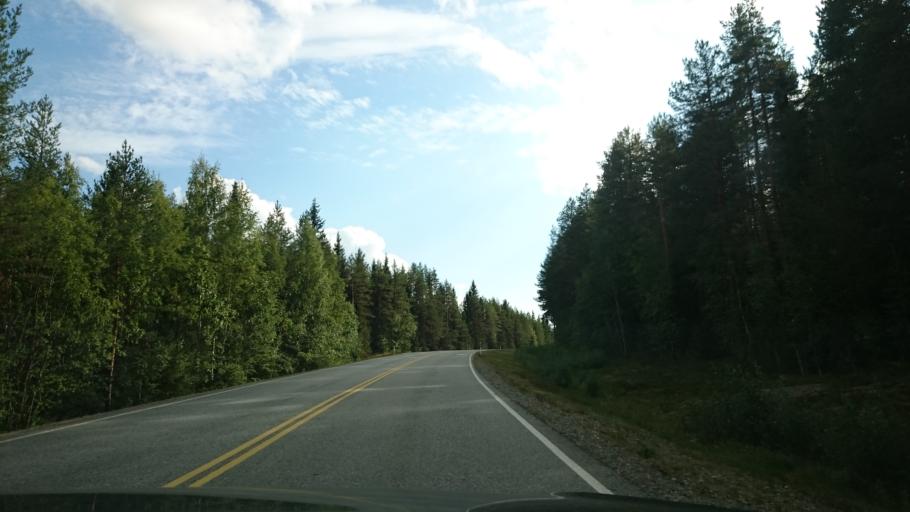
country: FI
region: Kainuu
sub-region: Kehys-Kainuu
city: Kuhmo
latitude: 64.5170
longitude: 29.9451
